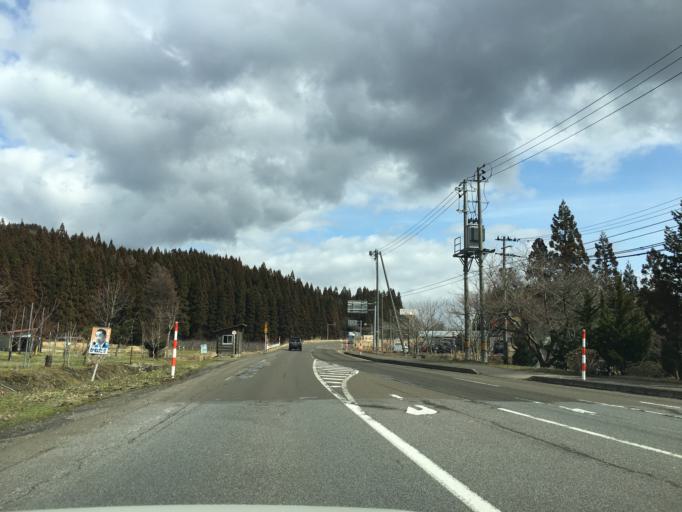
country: JP
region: Akita
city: Odate
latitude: 40.2165
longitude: 140.6278
